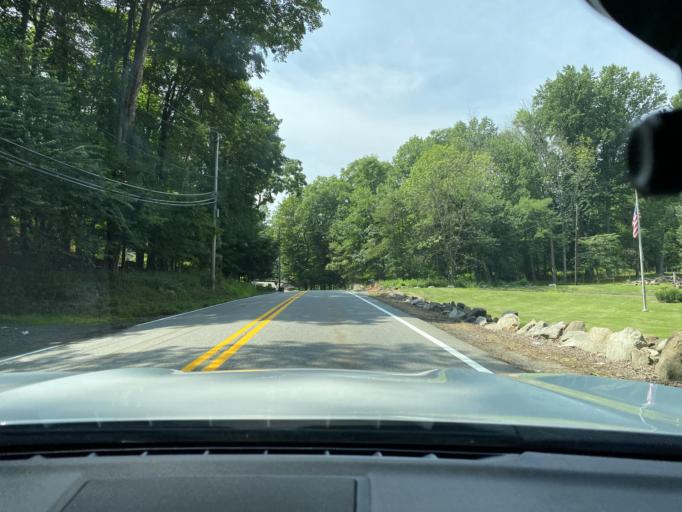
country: US
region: New Jersey
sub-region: Bergen County
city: Mahwah
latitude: 41.0759
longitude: -74.1945
